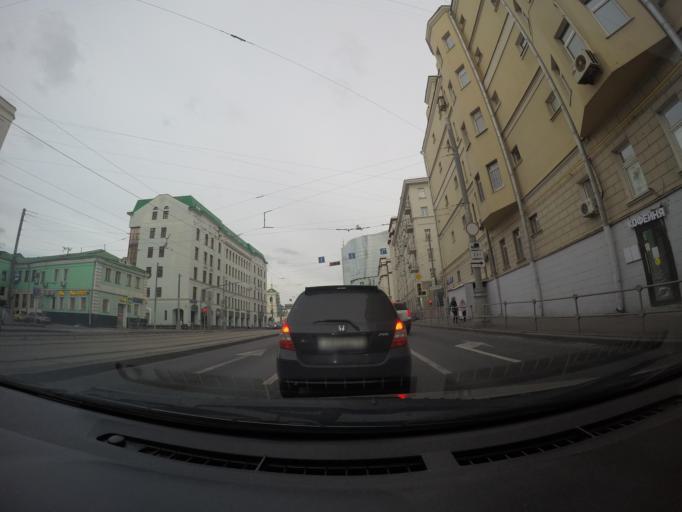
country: RU
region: Moskovskaya
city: Bogorodskoye
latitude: 55.7970
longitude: 37.7093
